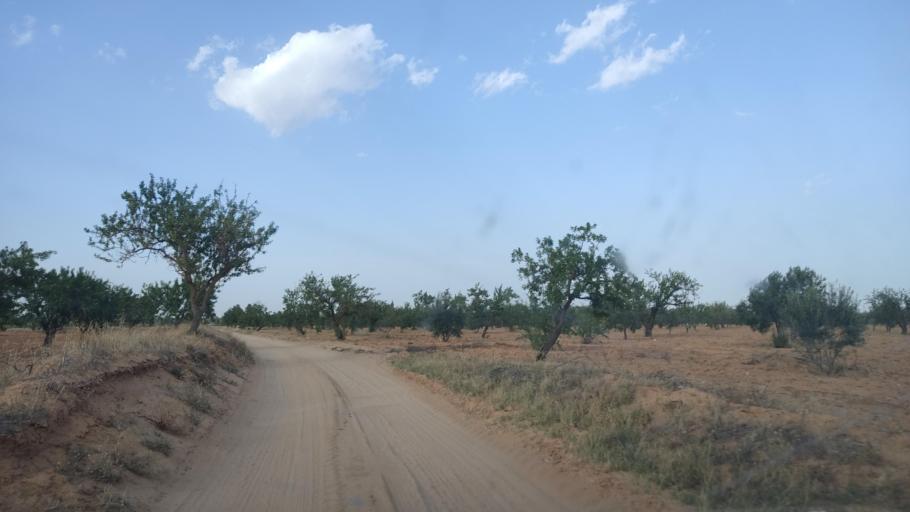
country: TN
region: Safaqis
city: Sfax
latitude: 34.8567
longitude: 10.5983
